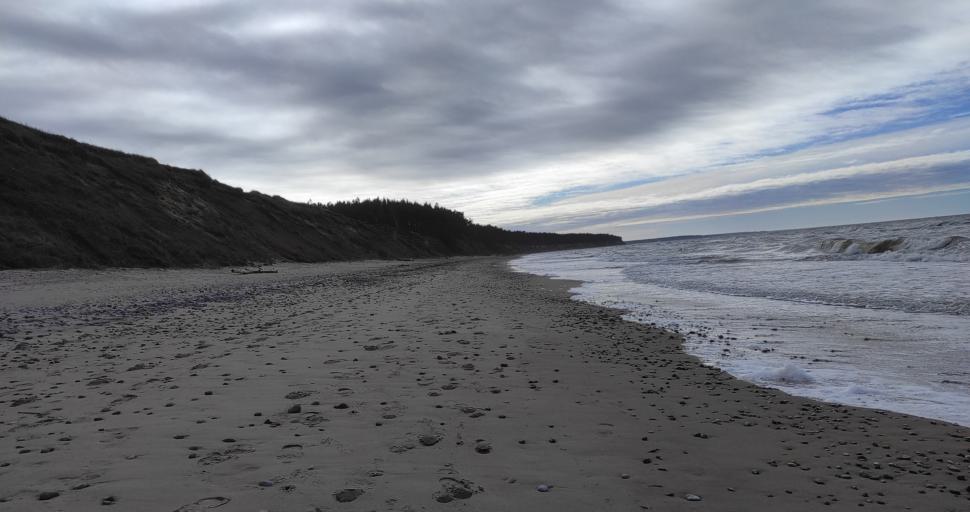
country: LV
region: Alsunga
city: Alsunga
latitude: 57.0354
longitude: 21.4012
